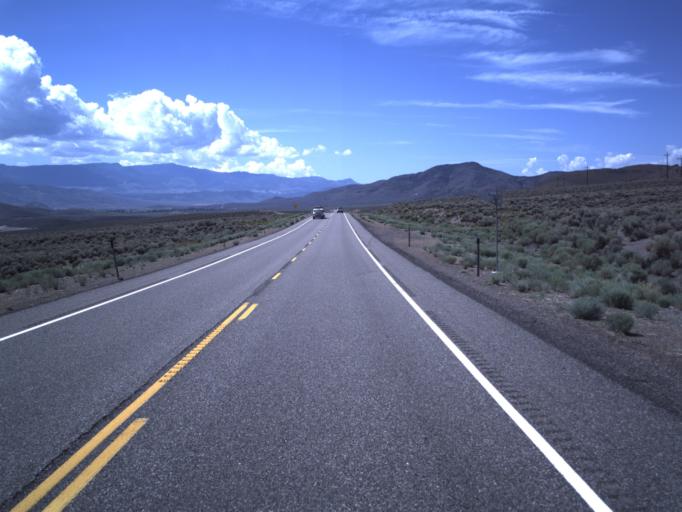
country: US
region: Utah
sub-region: Piute County
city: Junction
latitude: 38.3151
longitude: -112.2213
